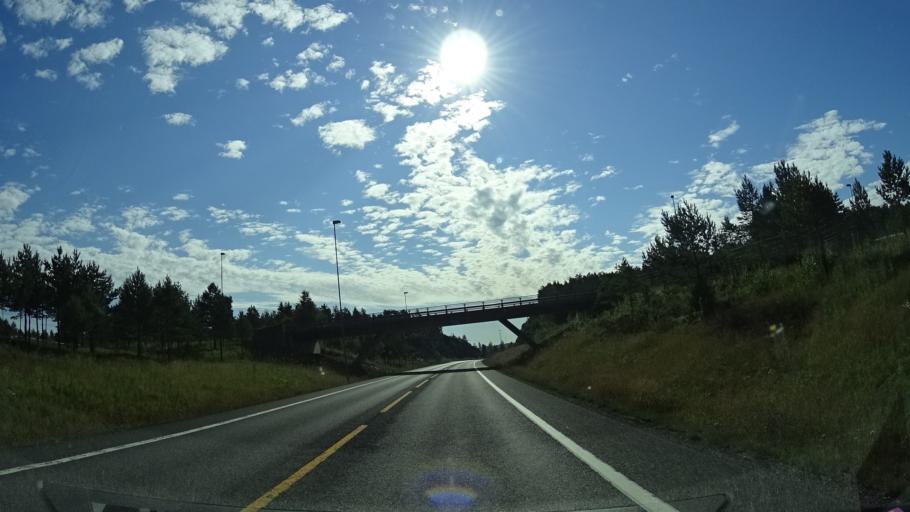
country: NO
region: Ostfold
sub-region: Marker
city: Orje
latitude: 59.5399
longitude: 11.5365
